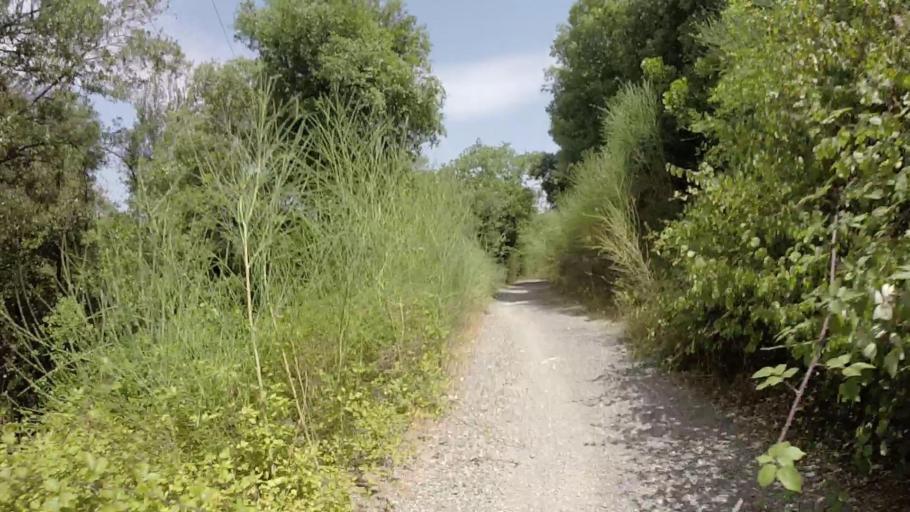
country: FR
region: Provence-Alpes-Cote d'Azur
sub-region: Departement des Alpes-Maritimes
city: Valbonne
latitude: 43.6204
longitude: 7.0232
